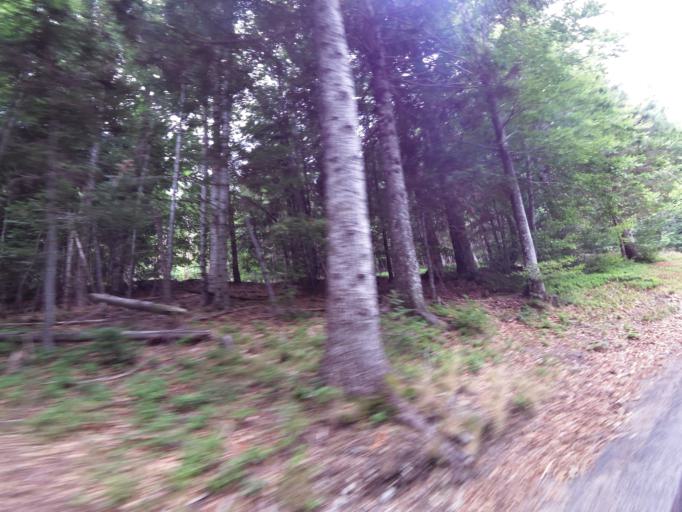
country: FR
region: Languedoc-Roussillon
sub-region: Departement du Gard
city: Valleraugue
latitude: 44.0680
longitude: 3.5906
